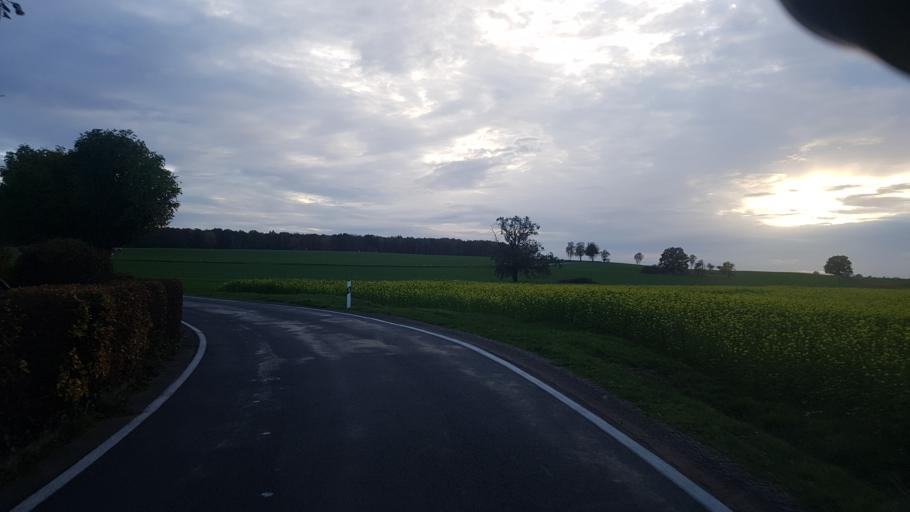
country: DE
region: Saxony
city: Dahlen
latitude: 51.3818
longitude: 13.0354
